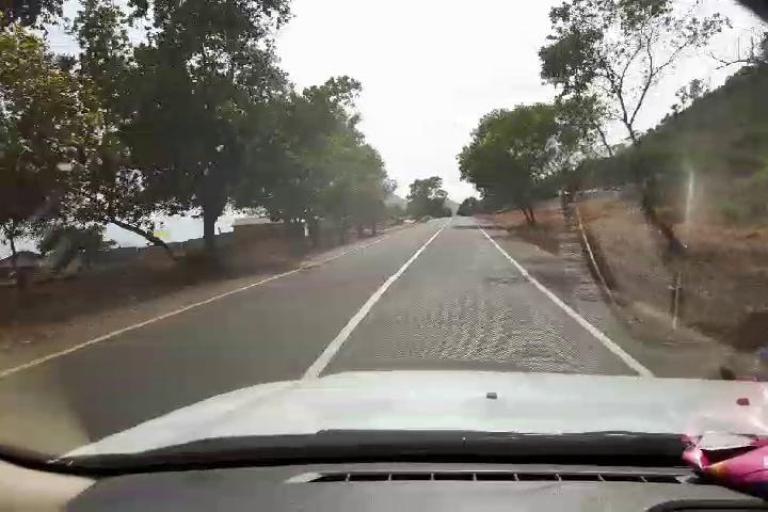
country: SL
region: Western Area
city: Waterloo
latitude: 8.2022
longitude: -13.1194
